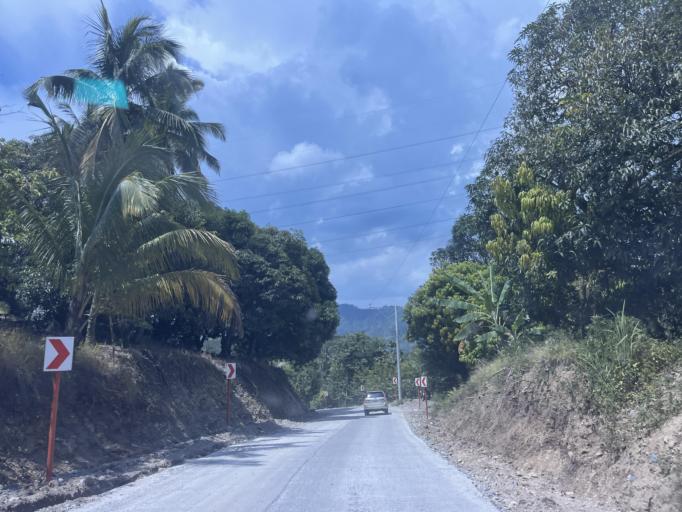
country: PH
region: Davao
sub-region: Province of Davao del Sur
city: Tamugan
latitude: 7.2858
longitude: 125.3380
